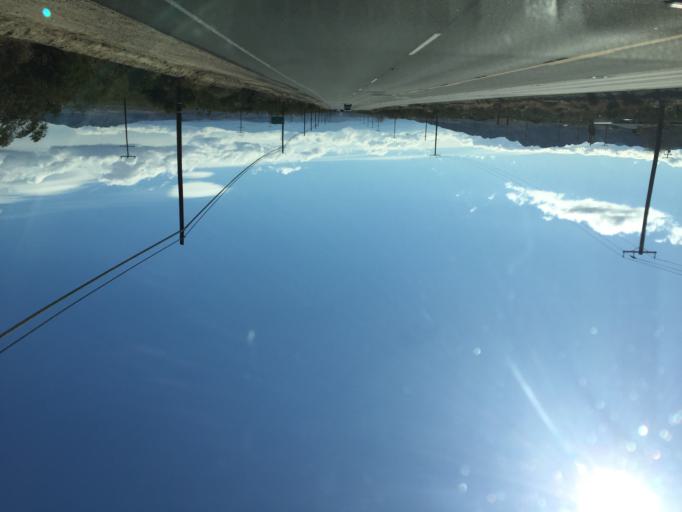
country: US
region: California
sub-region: San Bernardino County
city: Joshua Tree
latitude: 34.1353
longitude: -116.2228
